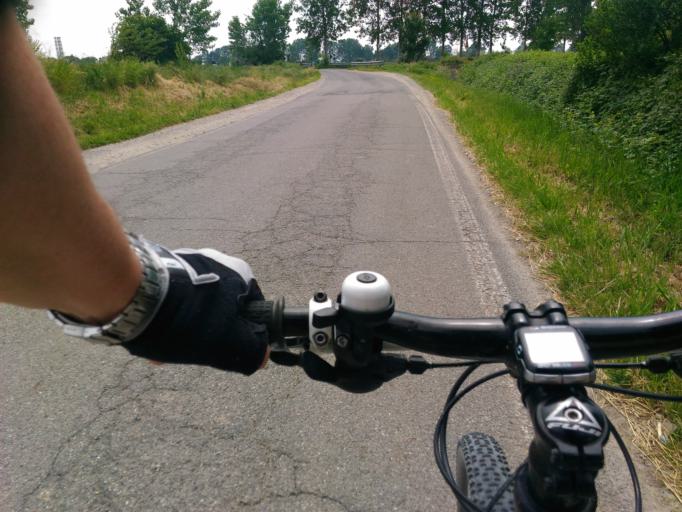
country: IT
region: Lombardy
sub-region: Provincia di Lodi
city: Quartiano
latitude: 45.3444
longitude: 9.4120
